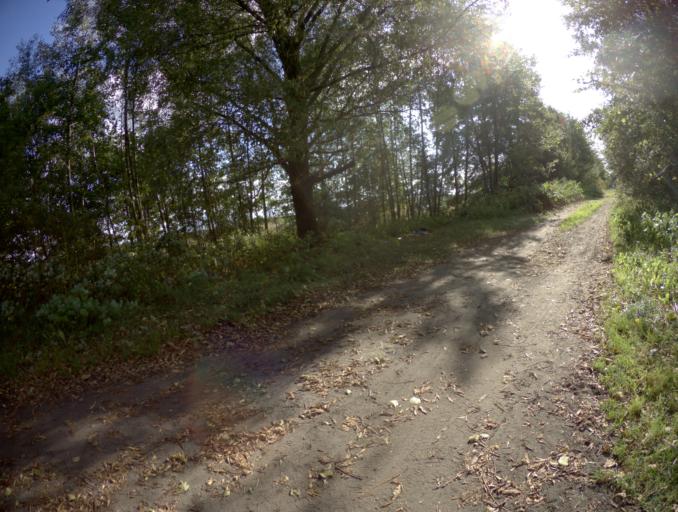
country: RU
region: Moskovskaya
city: Kerva
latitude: 55.6009
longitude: 39.5696
